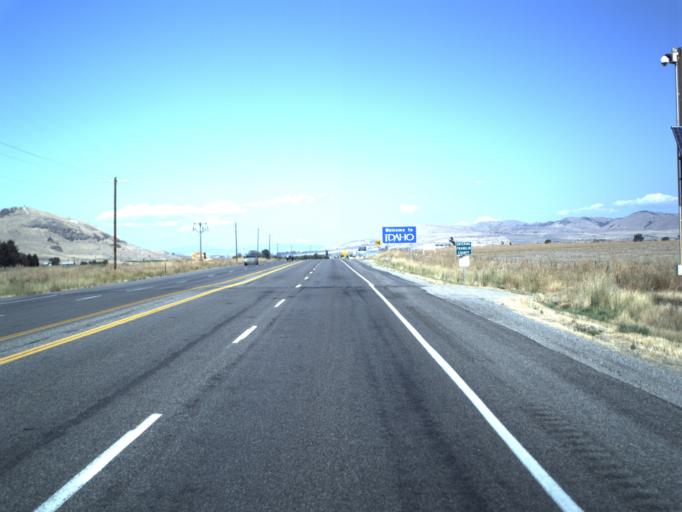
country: US
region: Utah
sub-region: Cache County
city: Lewiston
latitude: 41.9984
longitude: -111.8127
